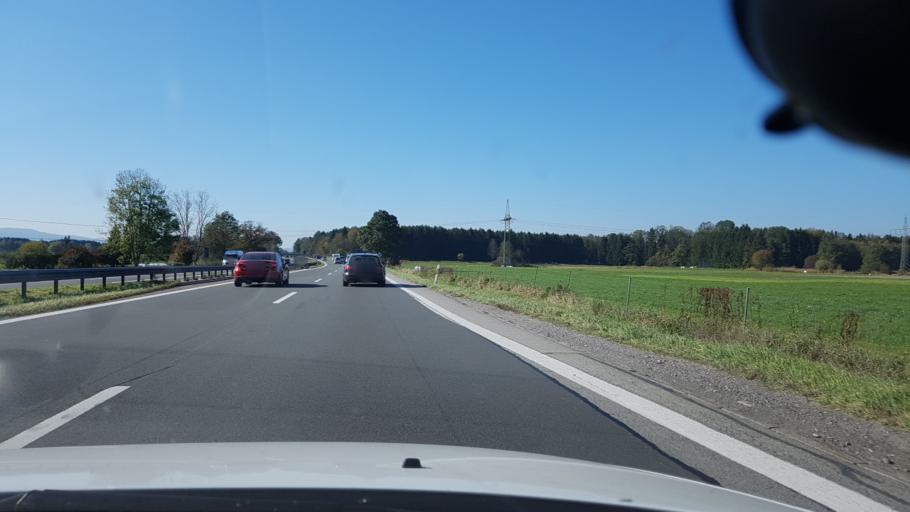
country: DE
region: Bavaria
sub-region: Upper Bavaria
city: Rohrdorf
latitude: 47.8044
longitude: 12.1583
